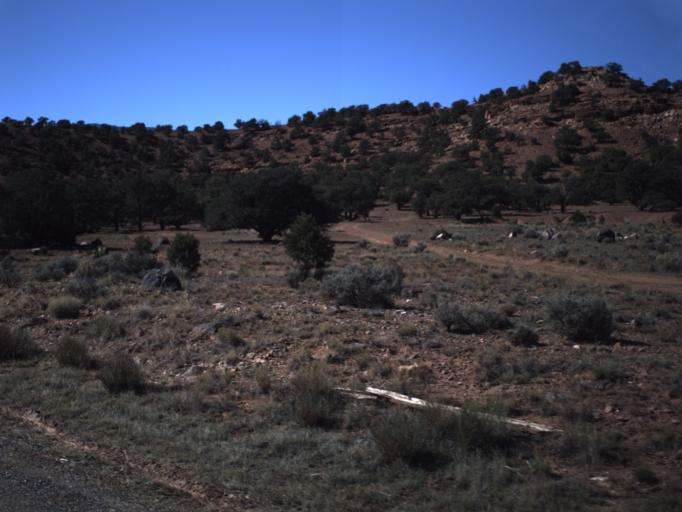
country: US
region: Utah
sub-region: Wayne County
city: Loa
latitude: 38.2534
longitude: -111.3788
